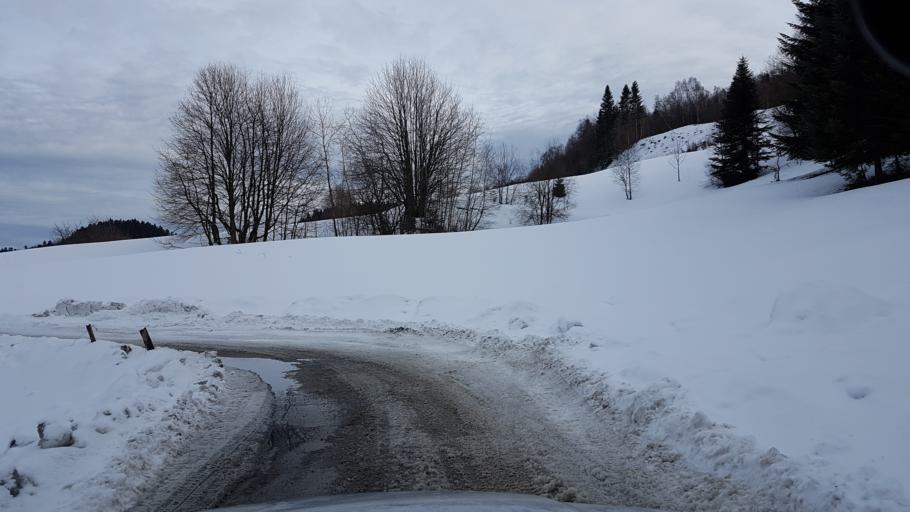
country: PL
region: Lesser Poland Voivodeship
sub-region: Powiat nowosadecki
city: Rytro
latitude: 49.4170
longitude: 20.6334
